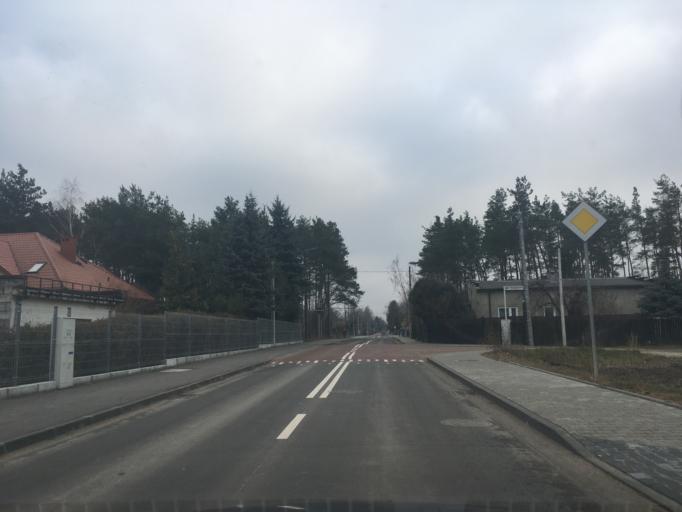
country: PL
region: Masovian Voivodeship
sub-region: Powiat piaseczynski
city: Piaseczno
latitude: 52.0630
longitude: 20.9769
